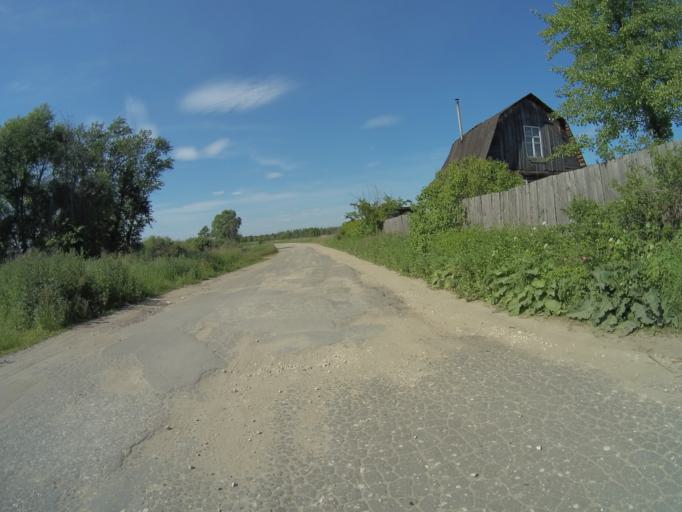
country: RU
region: Vladimir
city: Raduzhnyy
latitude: 56.0155
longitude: 40.3558
